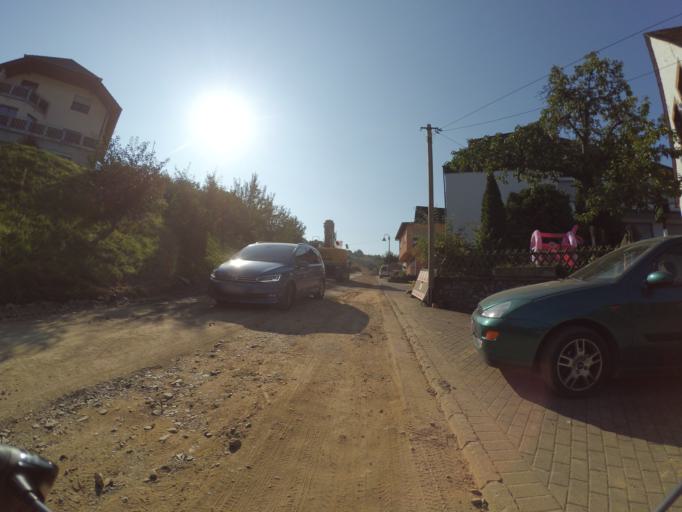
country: DE
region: Rheinland-Pfalz
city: Neumagen-Dhron
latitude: 49.8521
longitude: 6.8982
